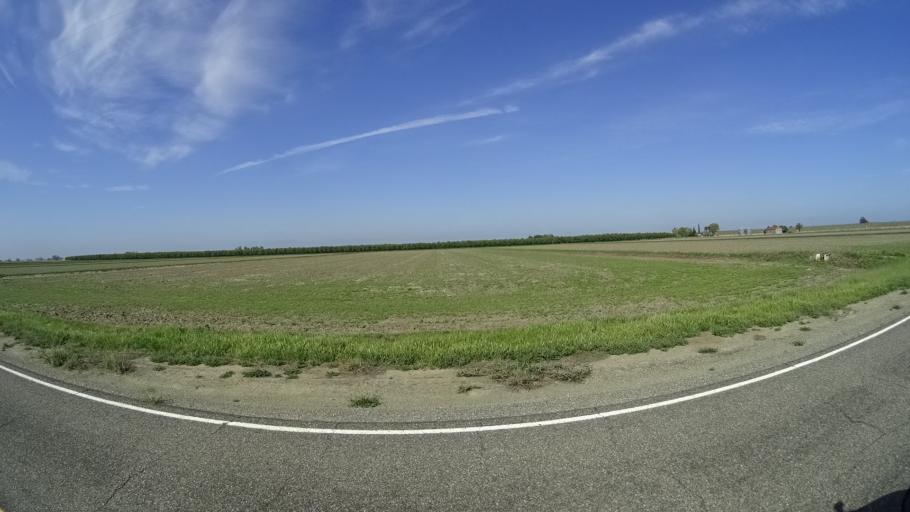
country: US
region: California
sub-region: Glenn County
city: Hamilton City
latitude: 39.6135
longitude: -122.0369
